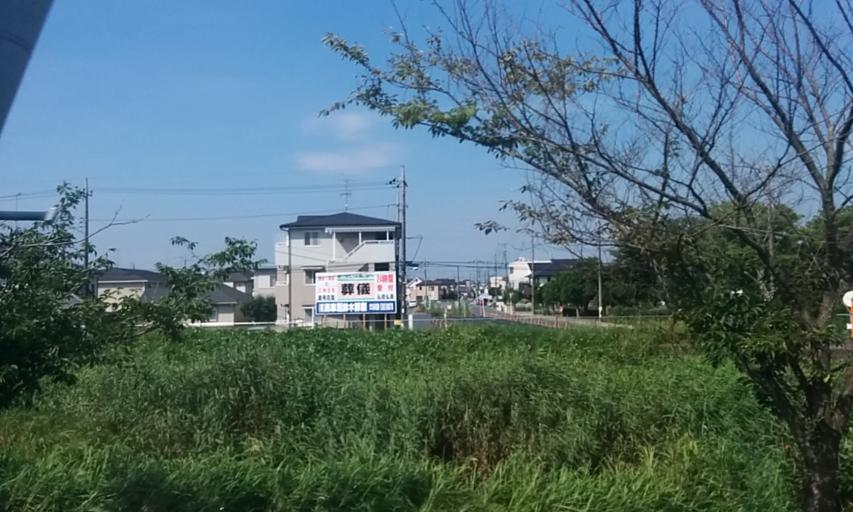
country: JP
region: Saitama
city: Kukichuo
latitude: 36.0976
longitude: 139.6556
